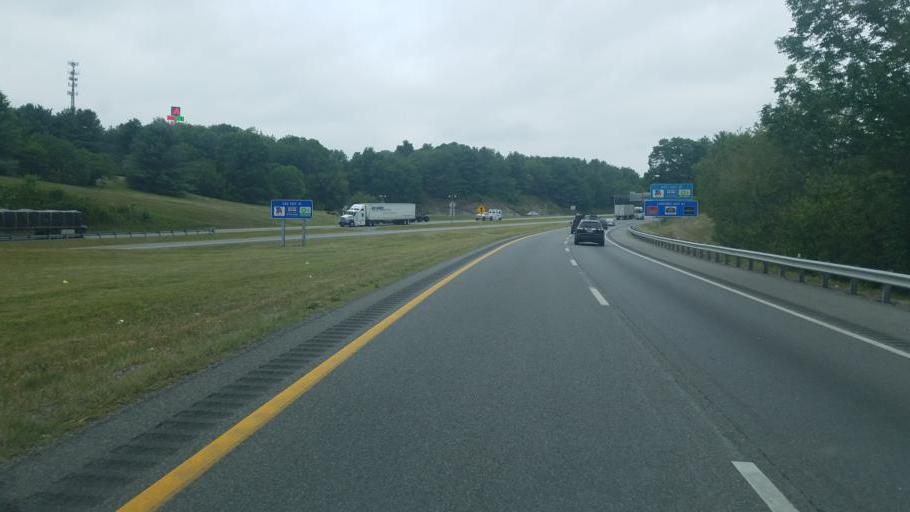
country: US
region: Virginia
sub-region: Wythe County
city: Wytheville
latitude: 36.9616
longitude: -81.0636
